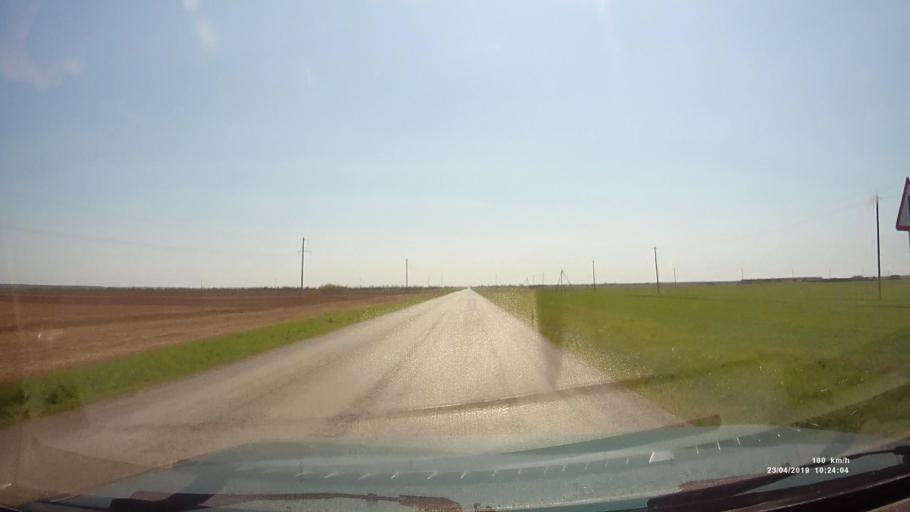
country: RU
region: Rostov
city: Sovetskoye
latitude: 46.6420
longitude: 42.4354
